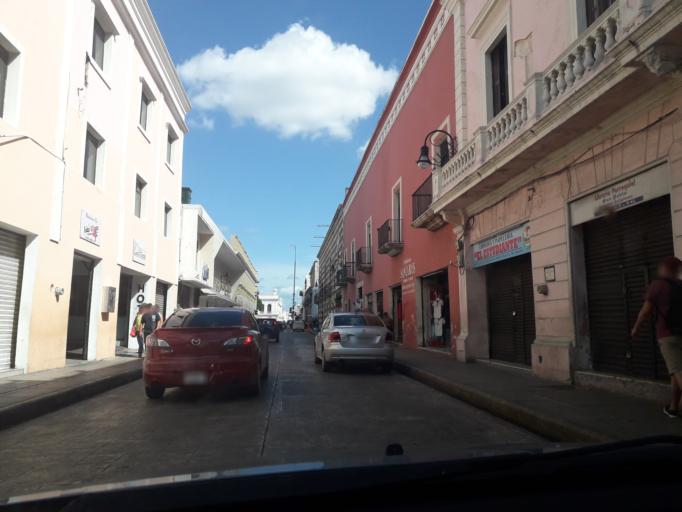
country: MX
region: Yucatan
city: Merida
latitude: 20.9667
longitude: -89.6253
